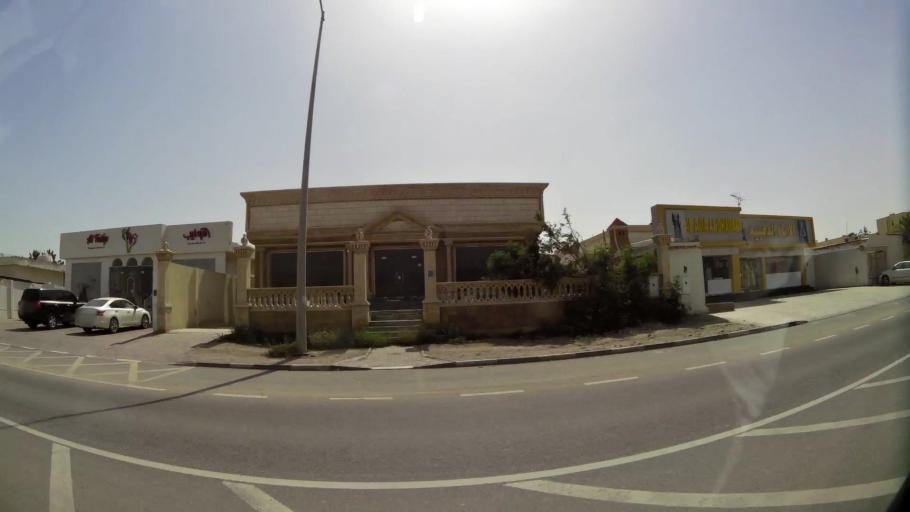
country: QA
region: Baladiyat Umm Salal
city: Umm Salal Muhammad
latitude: 25.4000
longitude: 51.4225
